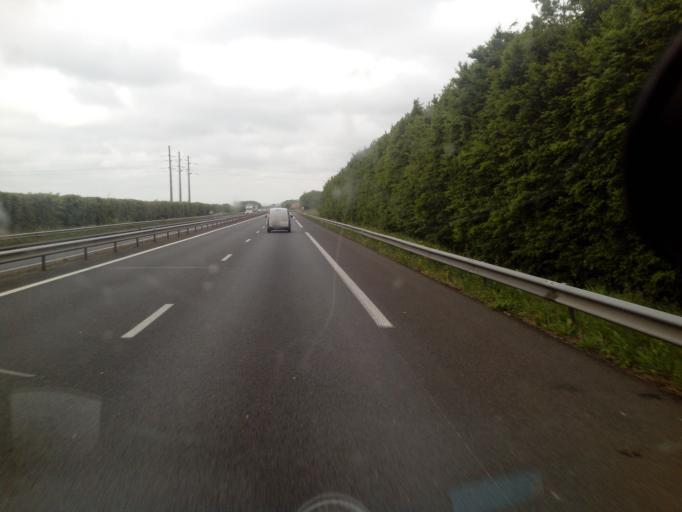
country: FR
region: Lower Normandy
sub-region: Departement du Calvados
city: Mouen
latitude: 49.1555
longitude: -0.4847
